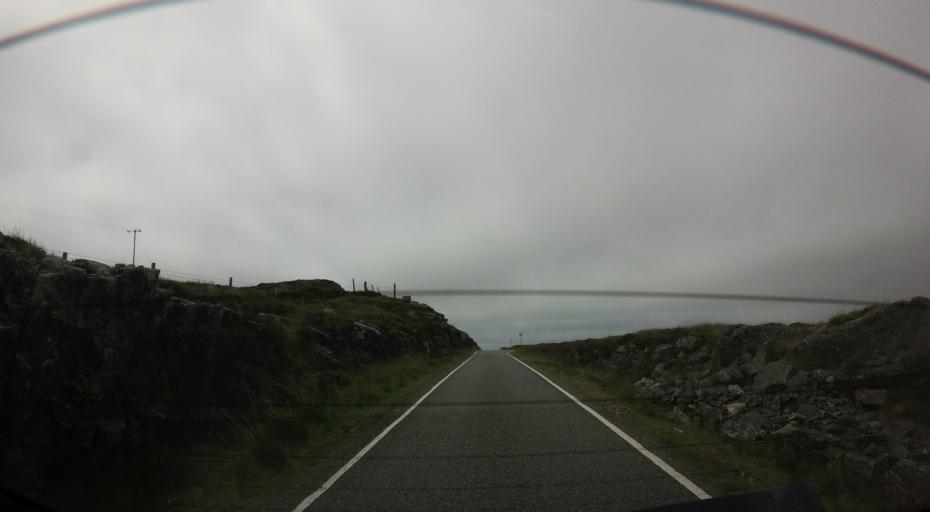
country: GB
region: Scotland
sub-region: Eilean Siar
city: Harris
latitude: 57.8680
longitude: -6.9060
